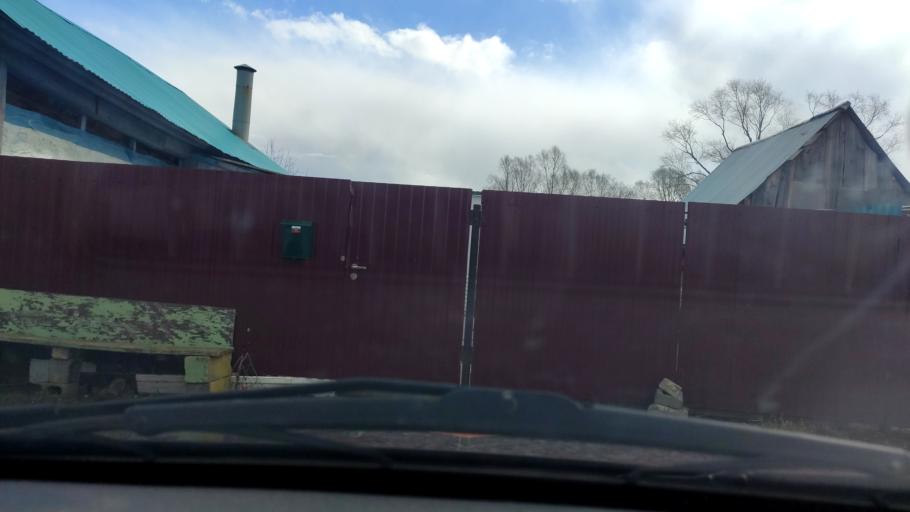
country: RU
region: Bashkortostan
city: Kabakovo
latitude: 54.6237
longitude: 56.1163
